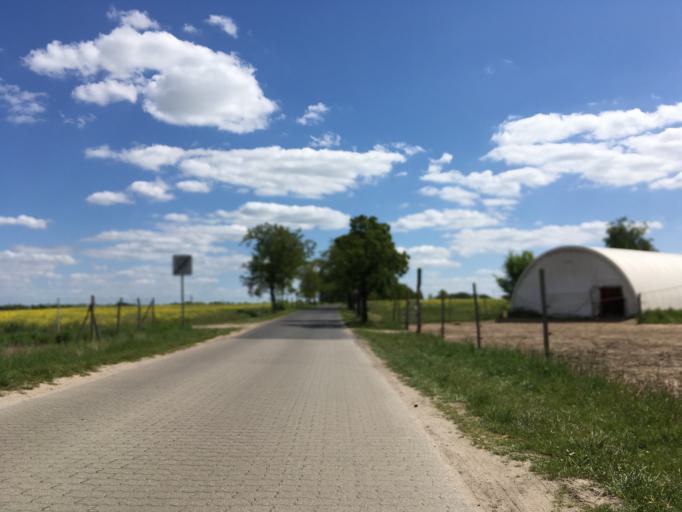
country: DE
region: Brandenburg
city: Biesenthal
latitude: 52.7425
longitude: 13.6539
